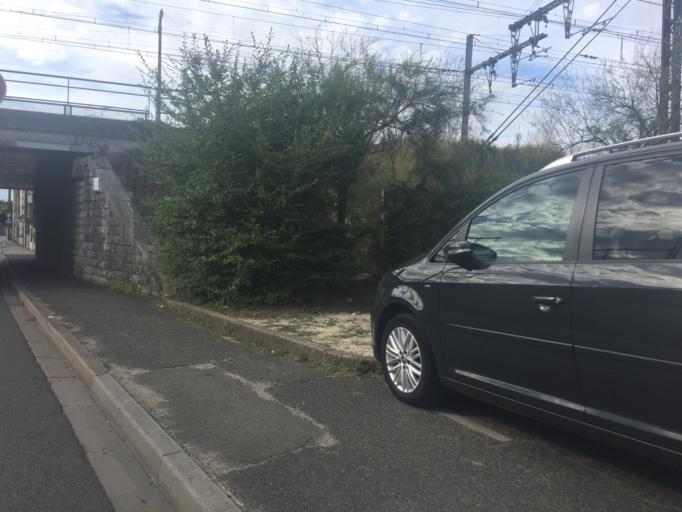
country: FR
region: Centre
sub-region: Departement d'Indre-et-Loire
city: Tours
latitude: 47.3802
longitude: 0.7082
